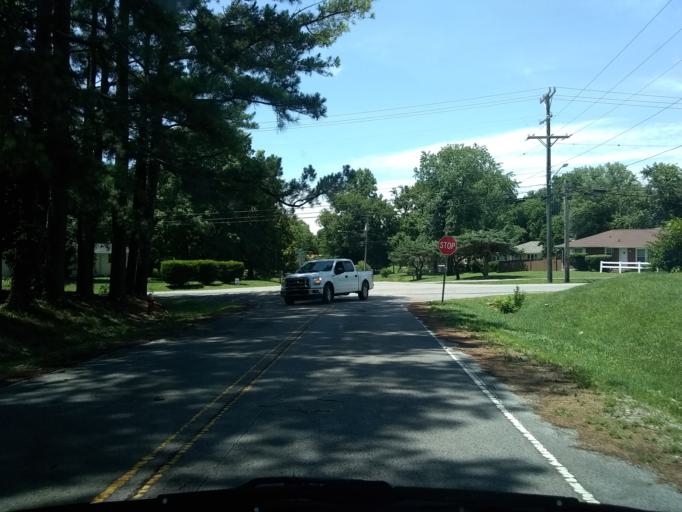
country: US
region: Tennessee
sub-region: Davidson County
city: Oak Hill
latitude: 36.1170
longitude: -86.7065
